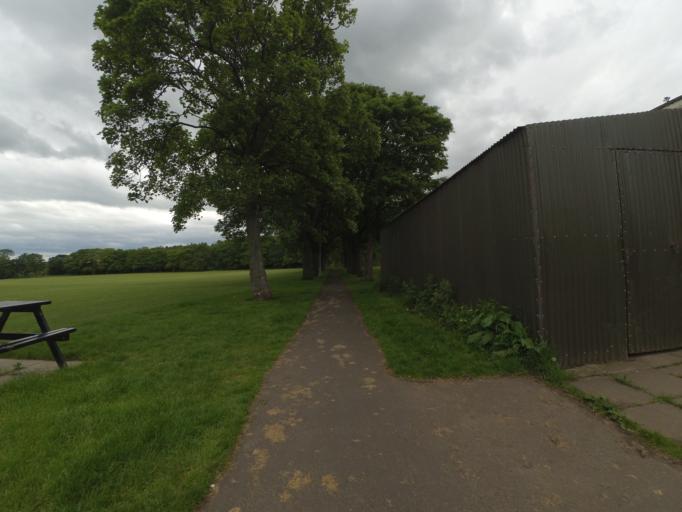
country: GB
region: Scotland
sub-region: East Lothian
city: Musselburgh
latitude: 55.9333
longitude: -3.0903
